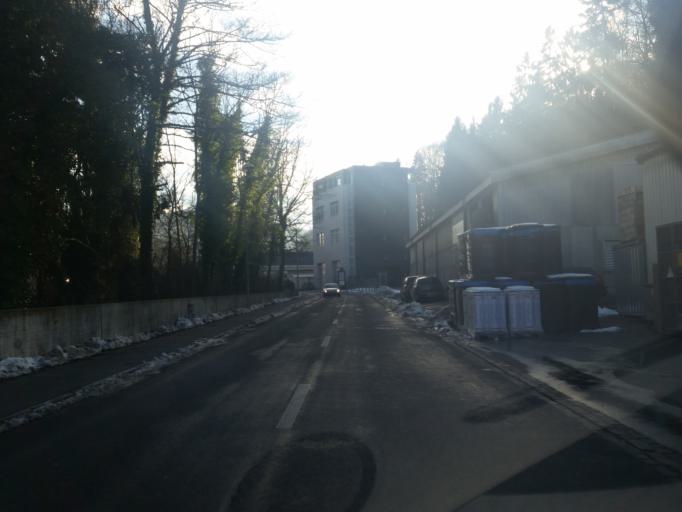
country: CH
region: Zurich
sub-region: Bezirk Dietikon
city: Dietikon / Kreuzacker
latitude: 47.3843
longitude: 8.3948
